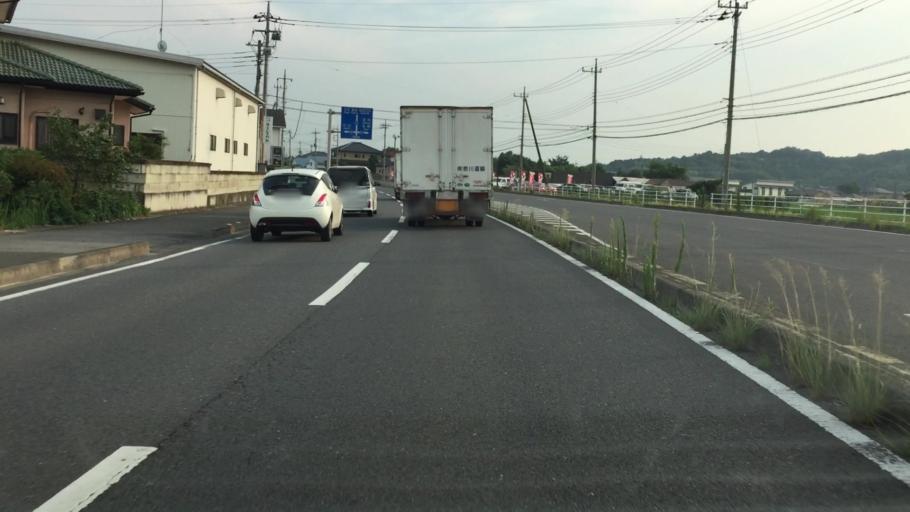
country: JP
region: Tochigi
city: Fujioka
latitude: 36.3222
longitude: 139.6778
